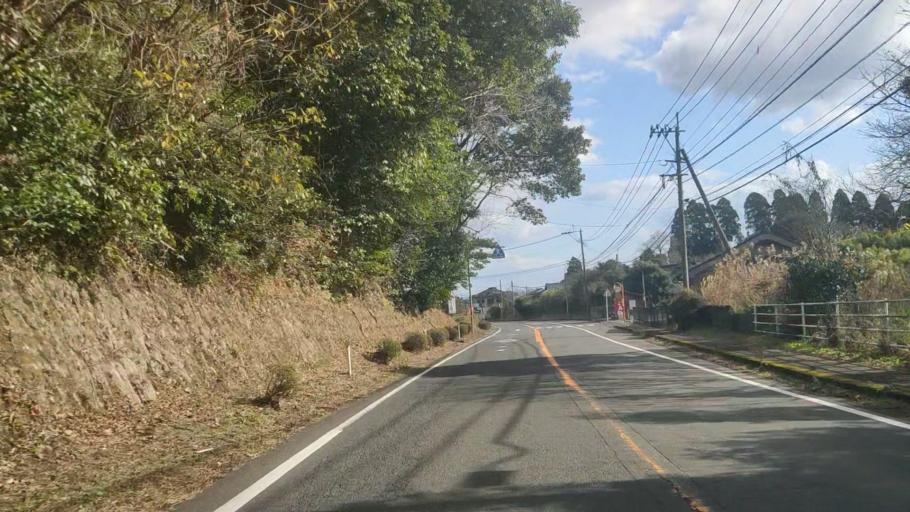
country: JP
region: Kagoshima
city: Kajiki
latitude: 31.8206
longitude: 130.6999
